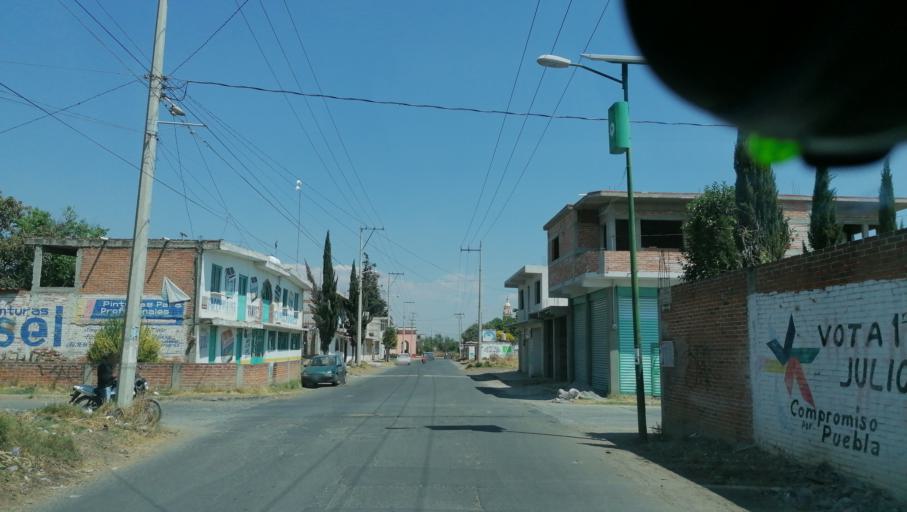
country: MX
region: Puebla
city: Huejotzingo
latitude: 19.1662
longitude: -98.4115
